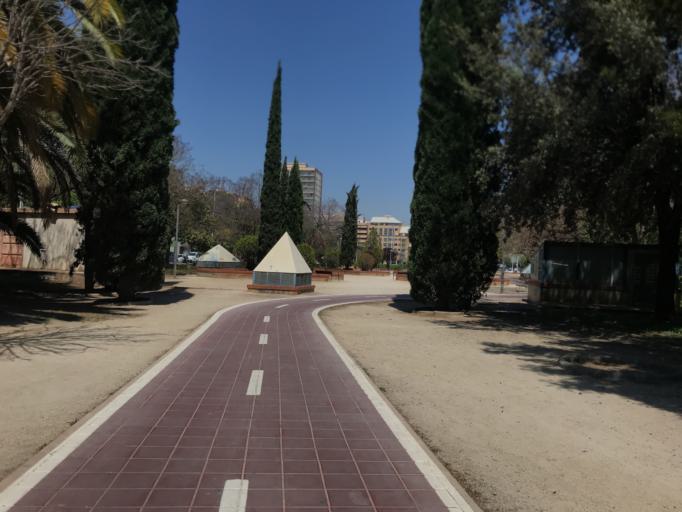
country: ES
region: Valencia
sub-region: Provincia de Valencia
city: Mislata
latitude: 39.4677
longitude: -0.4062
